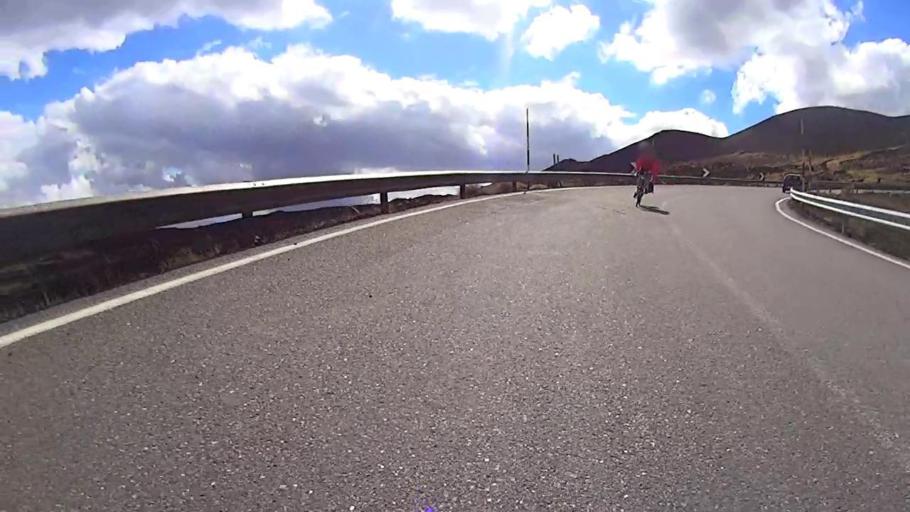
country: IT
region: Sicily
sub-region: Catania
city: Nicolosi
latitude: 37.6972
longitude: 15.0124
